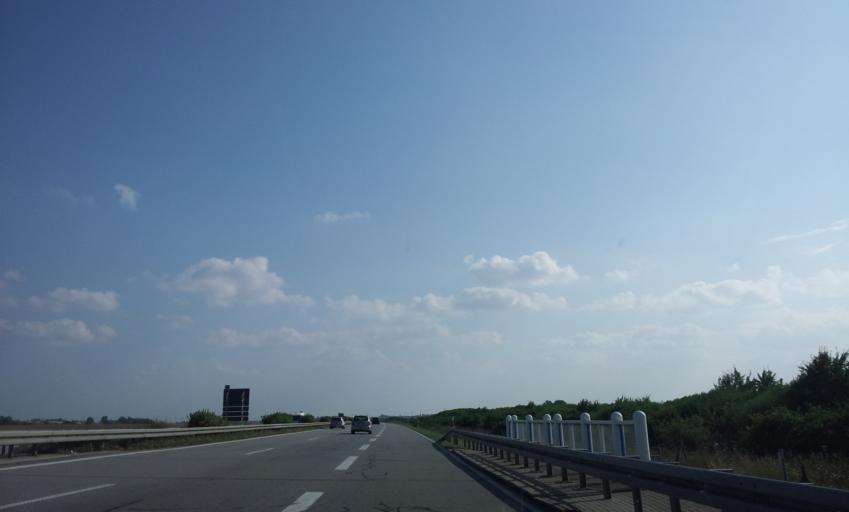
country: DE
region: Mecklenburg-Vorpommern
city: Jarmen
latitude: 53.8524
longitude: 13.3334
